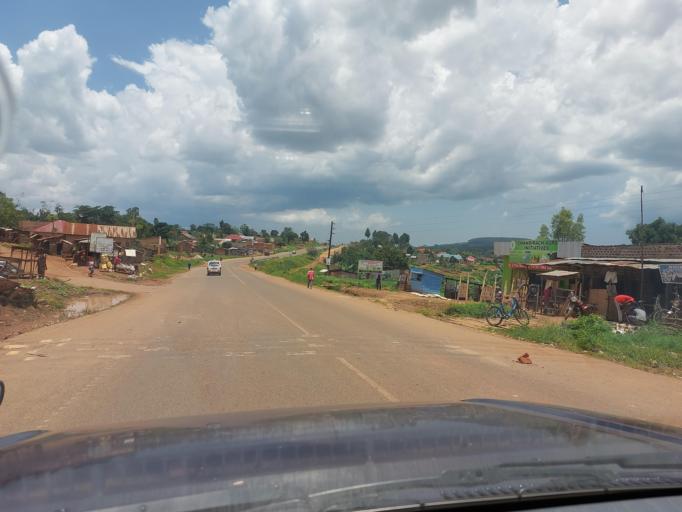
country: UG
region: Central Region
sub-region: Mukono District
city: Mukono
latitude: 0.3000
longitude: 32.7796
